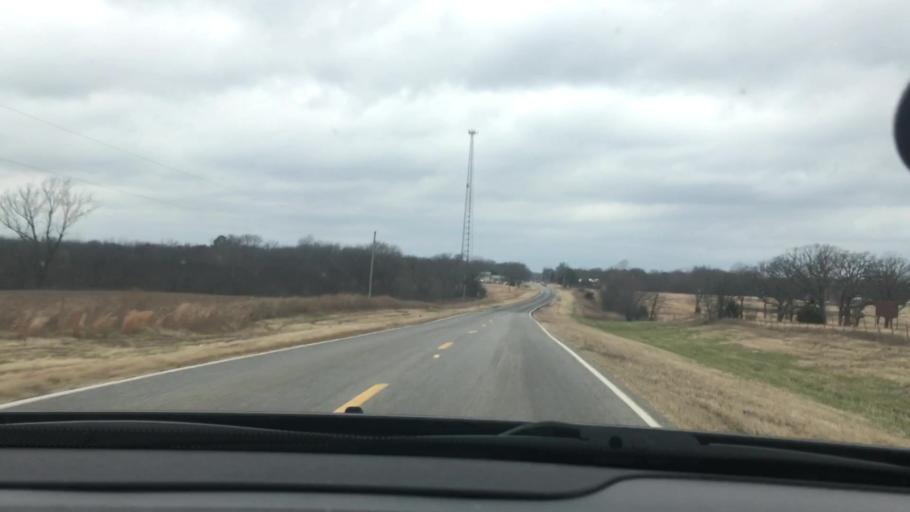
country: US
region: Oklahoma
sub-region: Coal County
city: Coalgate
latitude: 34.3749
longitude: -96.4101
